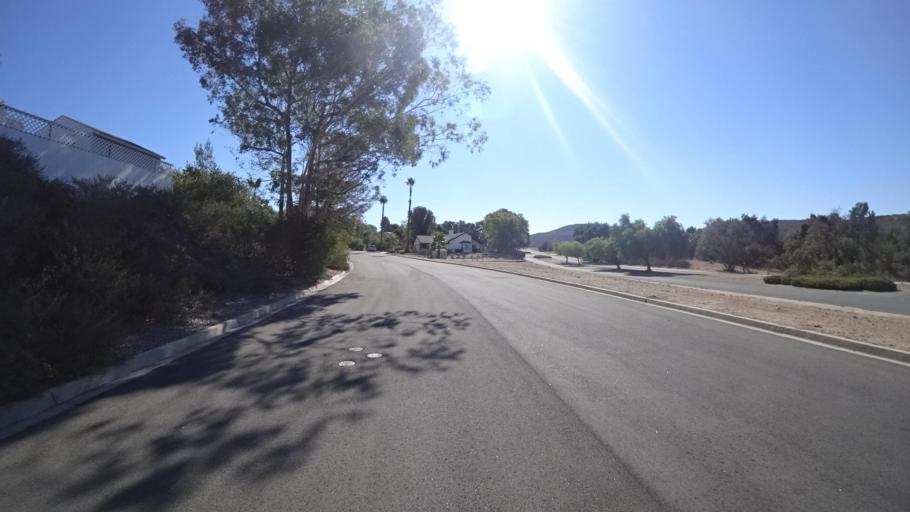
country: US
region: California
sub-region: San Diego County
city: San Diego Country Estates
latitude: 33.0040
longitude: -116.7754
